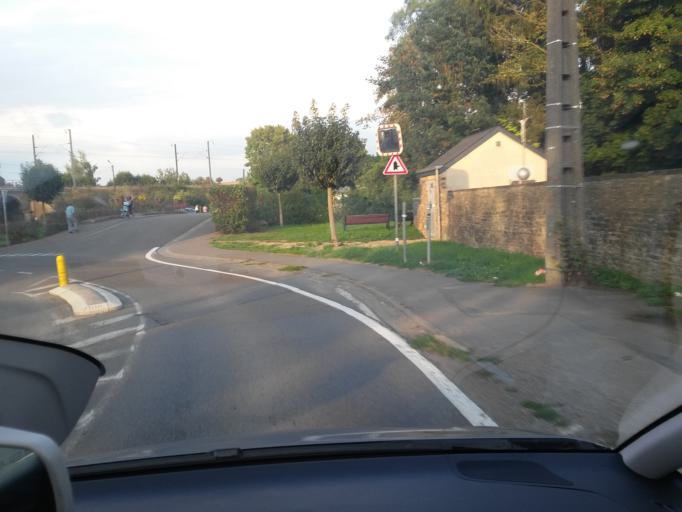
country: BE
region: Wallonia
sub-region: Province du Luxembourg
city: Virton
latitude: 49.5586
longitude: 5.5310
